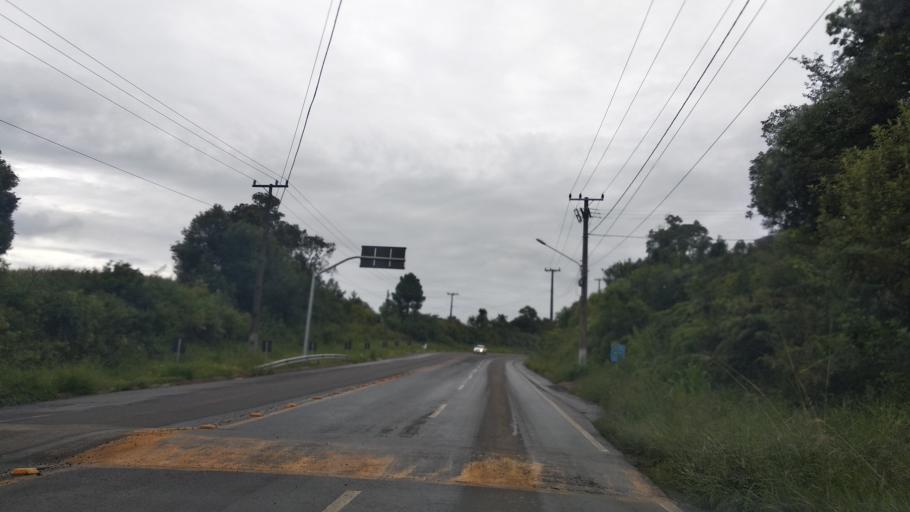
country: BR
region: Santa Catarina
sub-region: Videira
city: Videira
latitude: -27.0331
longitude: -51.1550
